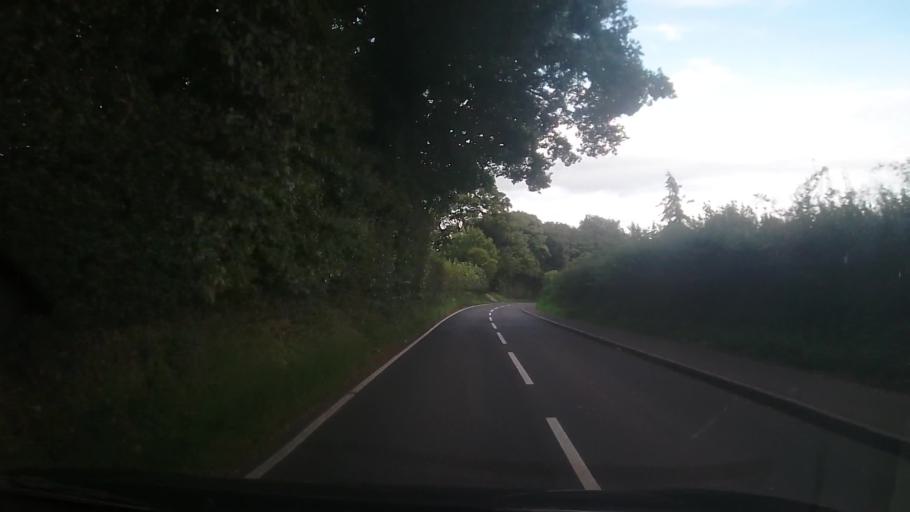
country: GB
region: England
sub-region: Shropshire
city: Bishop's Castle
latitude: 52.4960
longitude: -2.9907
